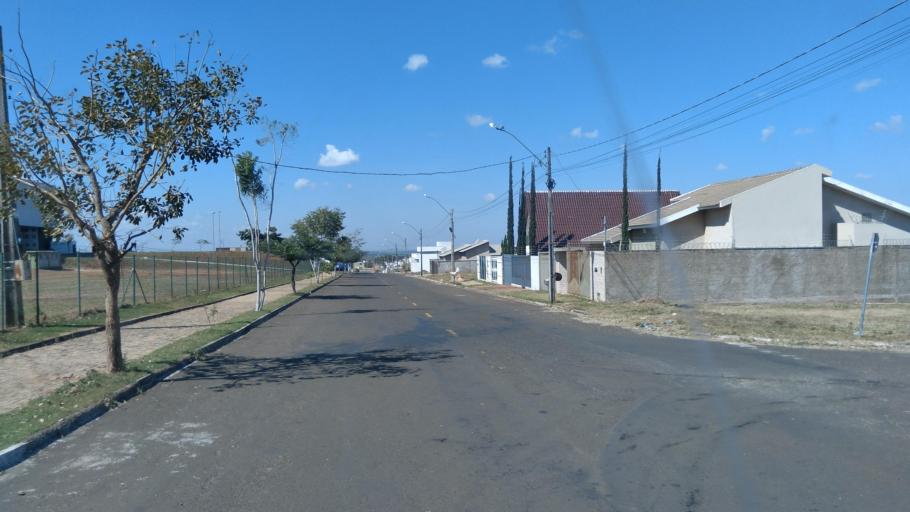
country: BR
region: Goias
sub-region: Mineiros
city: Mineiros
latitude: -17.5500
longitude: -52.5453
